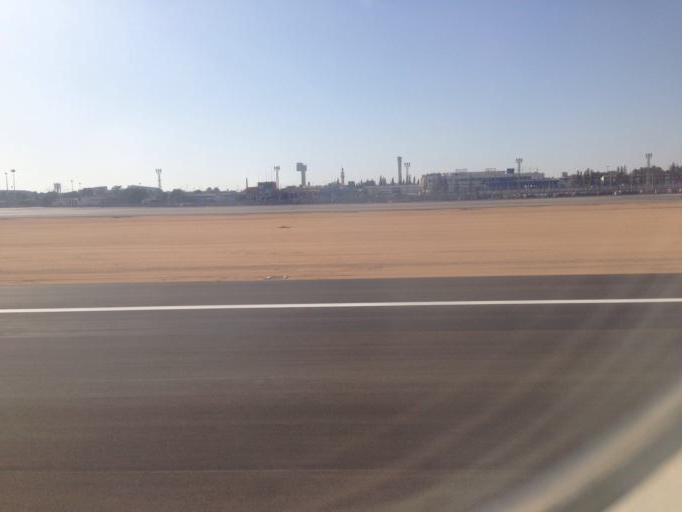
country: EG
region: Muhafazat al Qalyubiyah
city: Al Khankah
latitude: 30.1296
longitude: 31.3934
